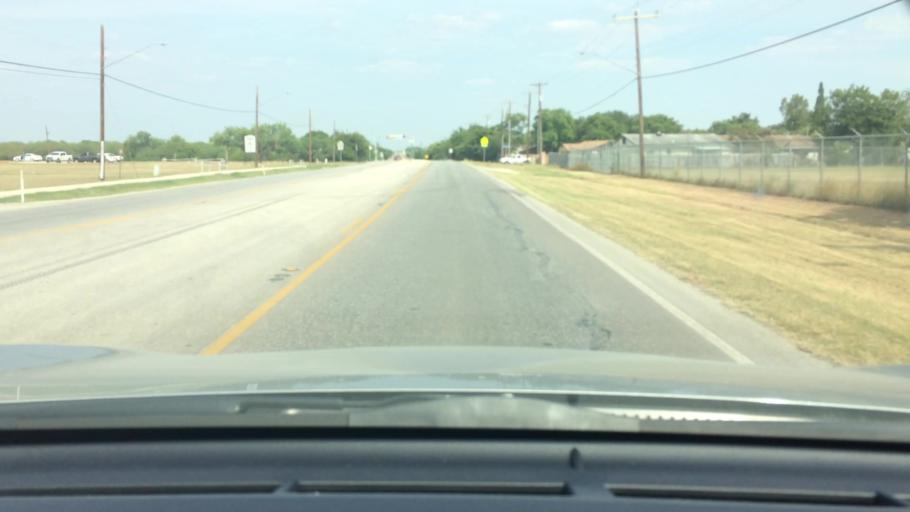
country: US
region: Texas
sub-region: Bexar County
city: China Grove
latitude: 29.3284
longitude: -98.4390
